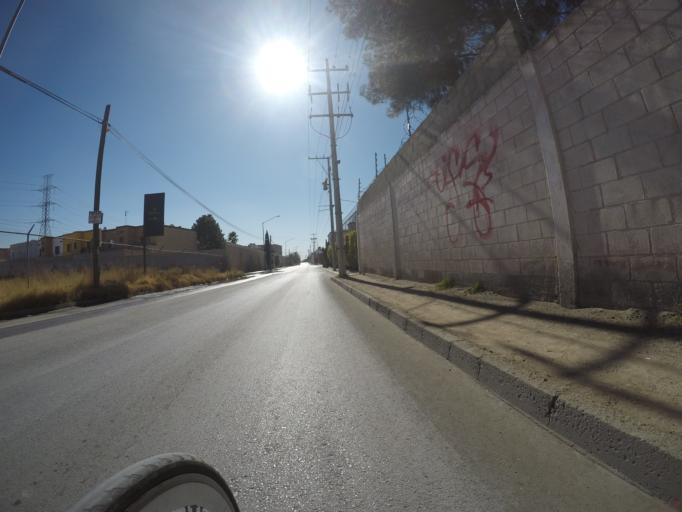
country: US
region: Texas
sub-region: El Paso County
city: Socorro
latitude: 31.6932
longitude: -106.3900
